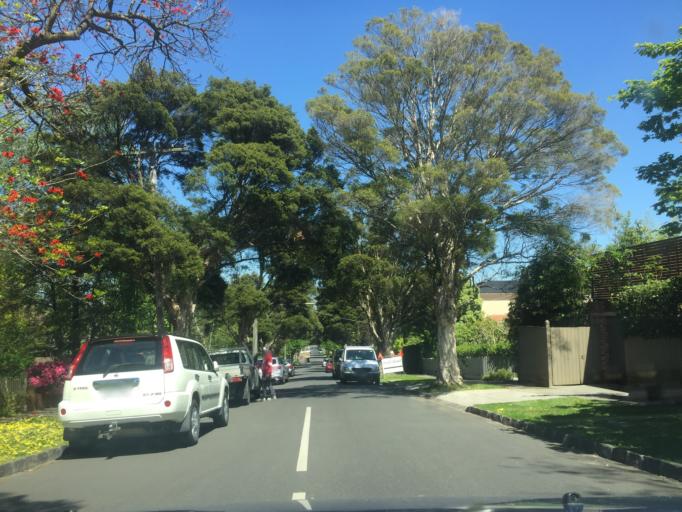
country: AU
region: Victoria
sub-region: Boroondara
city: Canterbury
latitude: -37.8204
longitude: 145.0769
